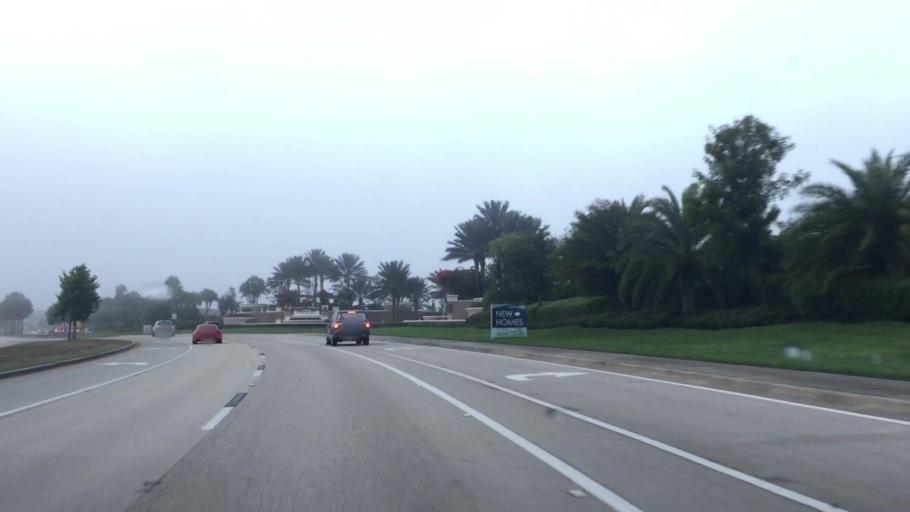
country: US
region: Florida
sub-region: Lee County
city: Gateway
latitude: 26.5730
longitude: -81.7813
